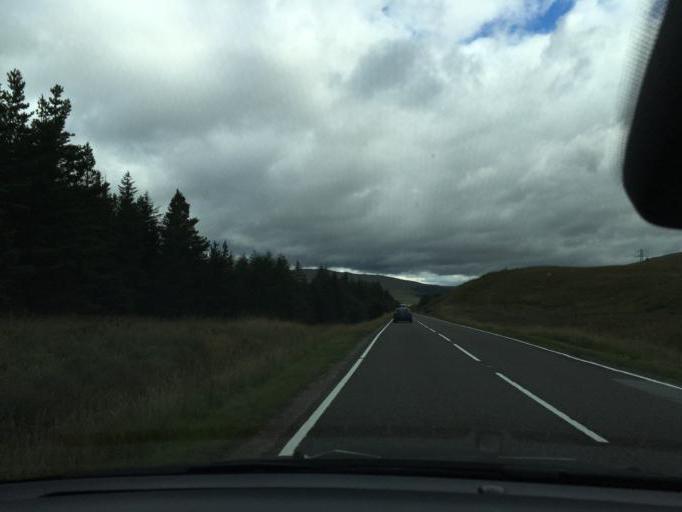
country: GB
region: Scotland
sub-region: Highland
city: Spean Bridge
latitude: 56.5416
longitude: -4.7642
